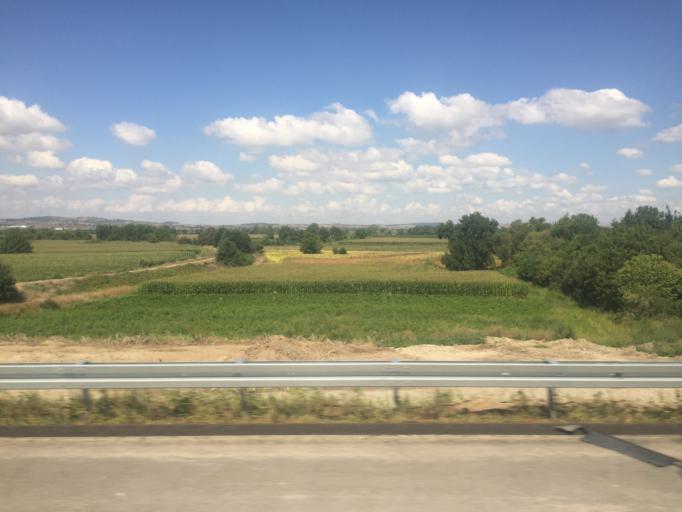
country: TR
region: Balikesir
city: Gobel
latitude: 40.0246
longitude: 28.2082
